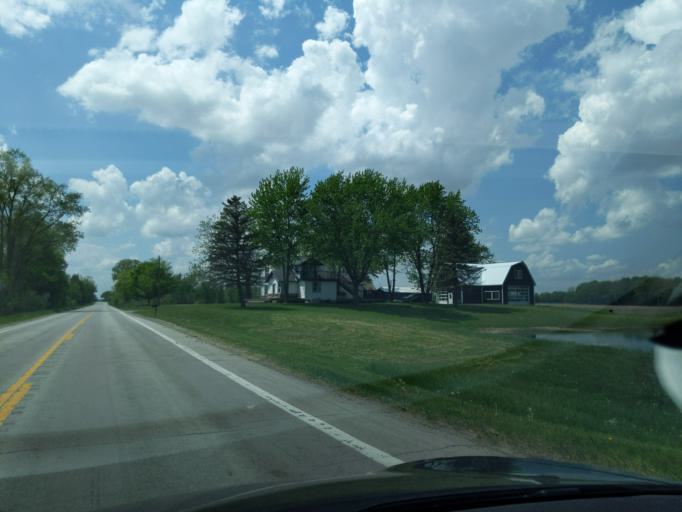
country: US
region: Michigan
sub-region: Ingham County
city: Stockbridge
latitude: 42.5559
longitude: -84.2410
